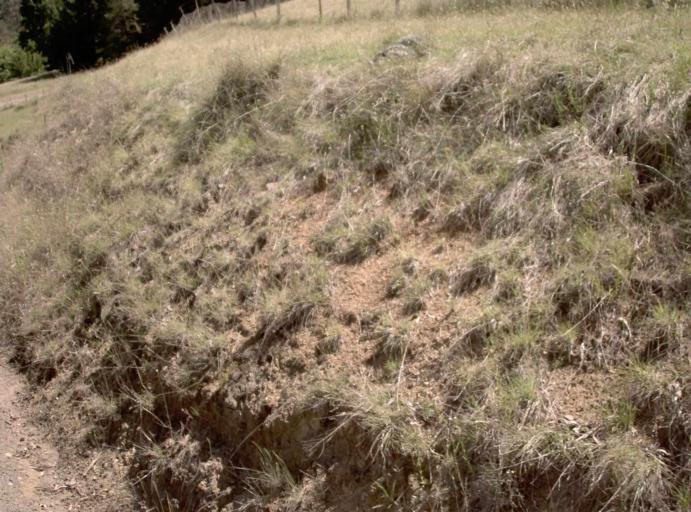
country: AU
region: New South Wales
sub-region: Bombala
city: Bombala
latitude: -37.1239
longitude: 148.6631
